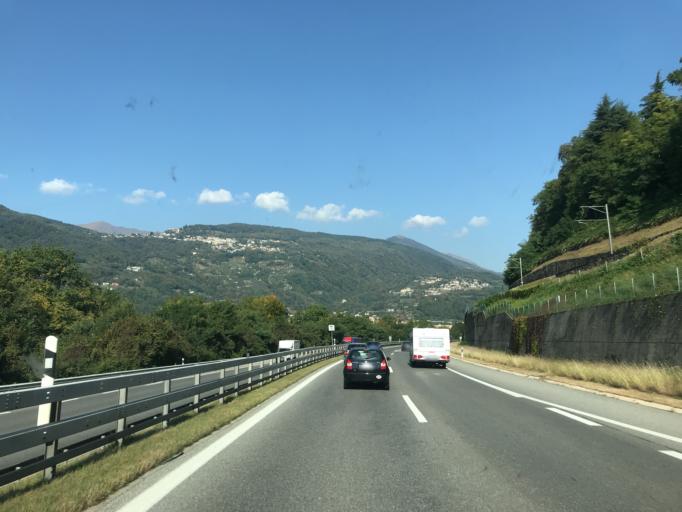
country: CH
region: Ticino
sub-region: Lugano District
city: Agno
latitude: 45.9977
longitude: 8.9159
